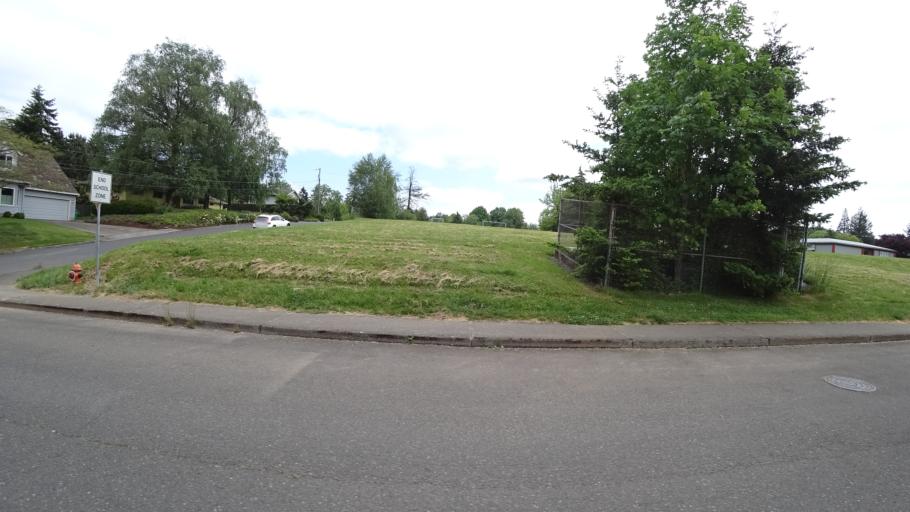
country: US
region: Oregon
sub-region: Clackamas County
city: Lake Oswego
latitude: 45.4418
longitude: -122.7051
